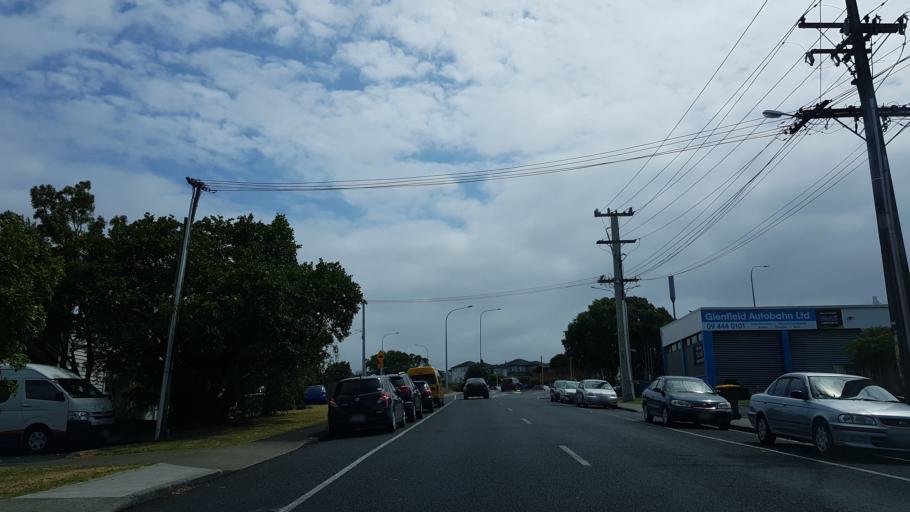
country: NZ
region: Auckland
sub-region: Auckland
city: North Shore
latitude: -36.7693
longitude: 174.7200
